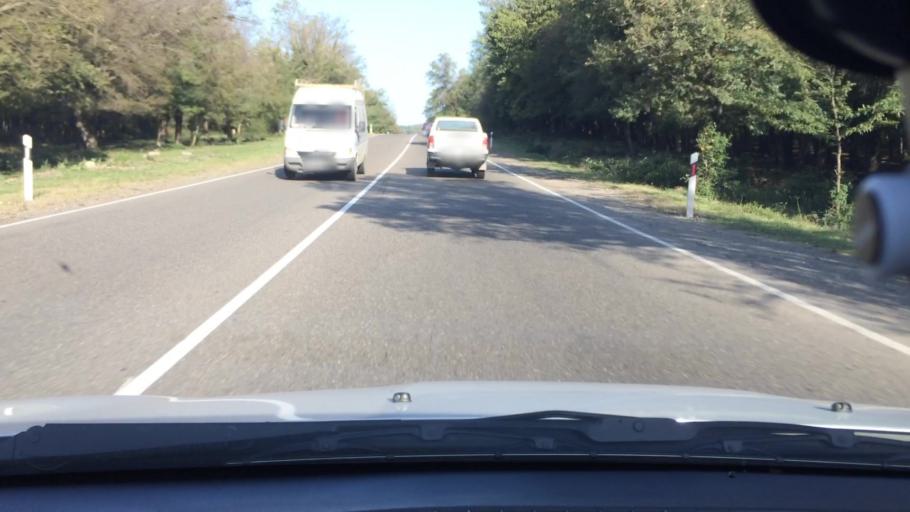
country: GE
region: Imereti
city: Kutaisi
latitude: 42.2334
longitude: 42.7742
